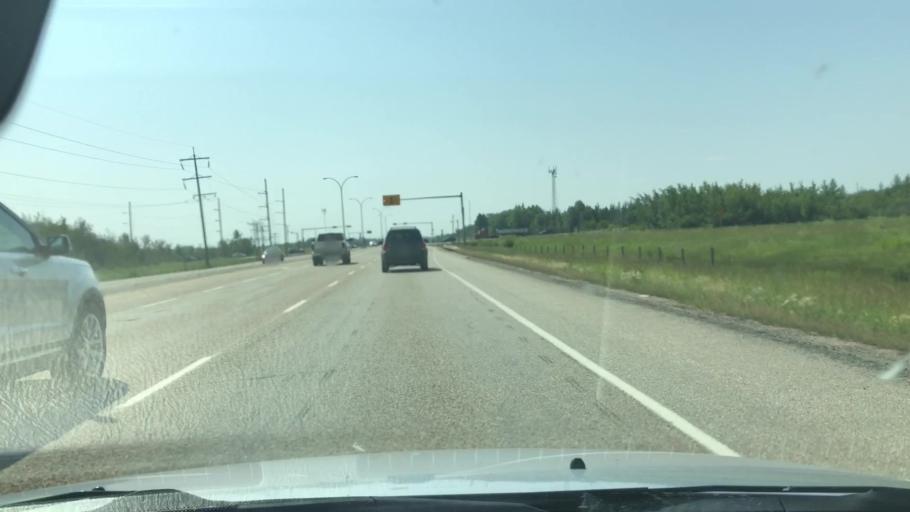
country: CA
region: Alberta
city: Devon
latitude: 53.4564
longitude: -113.7627
